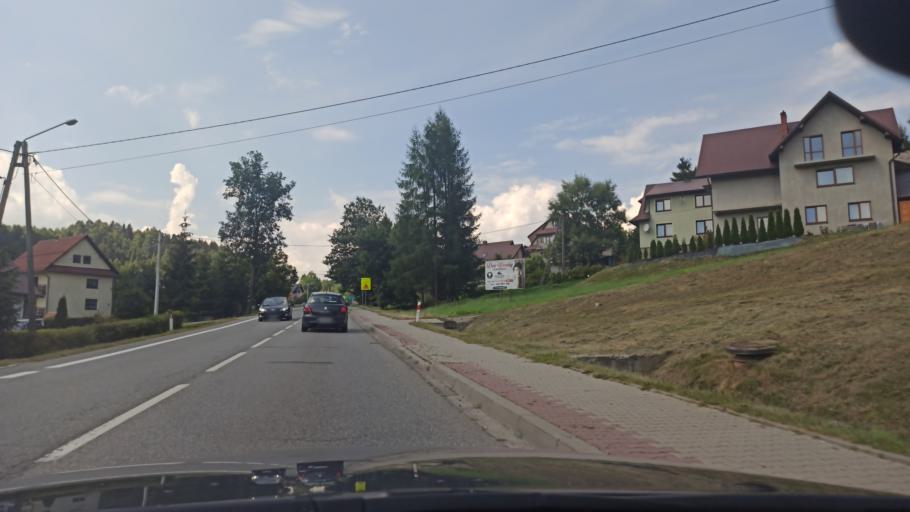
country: PL
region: Lesser Poland Voivodeship
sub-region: Powiat nowotarski
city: Krosnica
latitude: 49.4458
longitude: 20.3433
